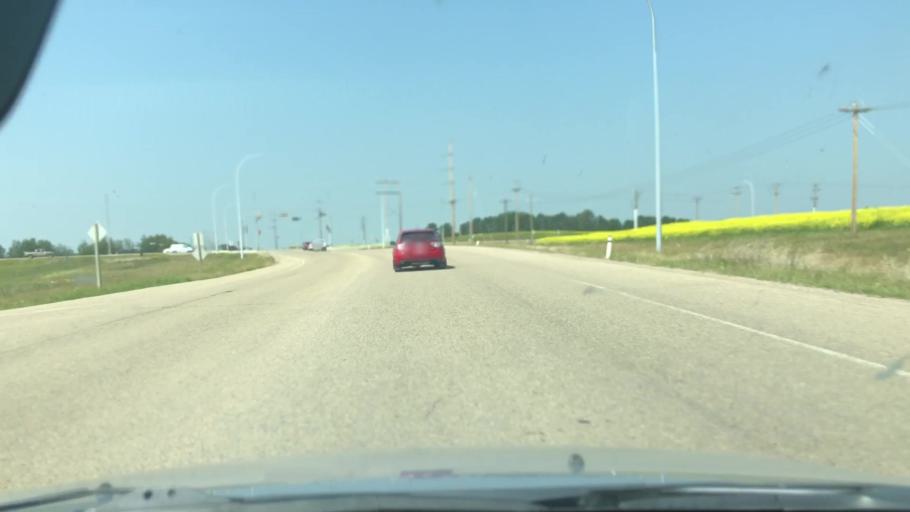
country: CA
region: Alberta
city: Devon
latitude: 53.5123
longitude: -113.7595
